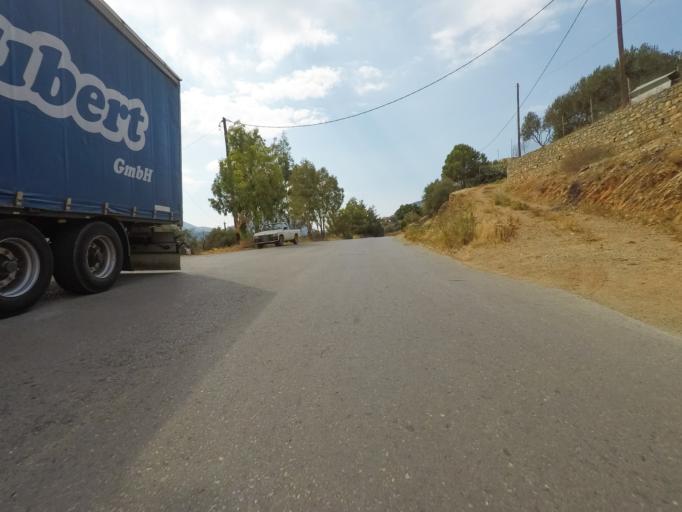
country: GR
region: Crete
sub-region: Nomos Lasithiou
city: Neapoli
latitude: 35.2609
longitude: 25.6107
